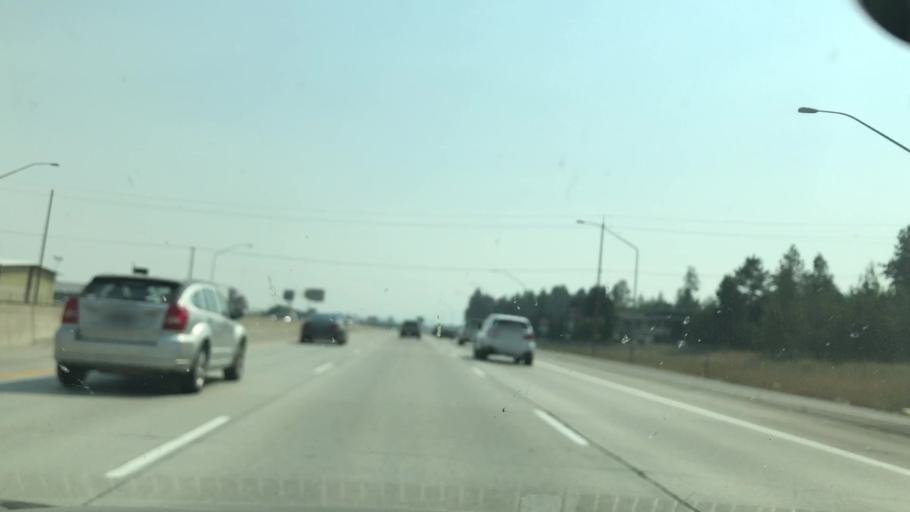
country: US
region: Washington
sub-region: Spokane County
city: Spokane Valley
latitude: 47.6739
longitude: -117.2365
